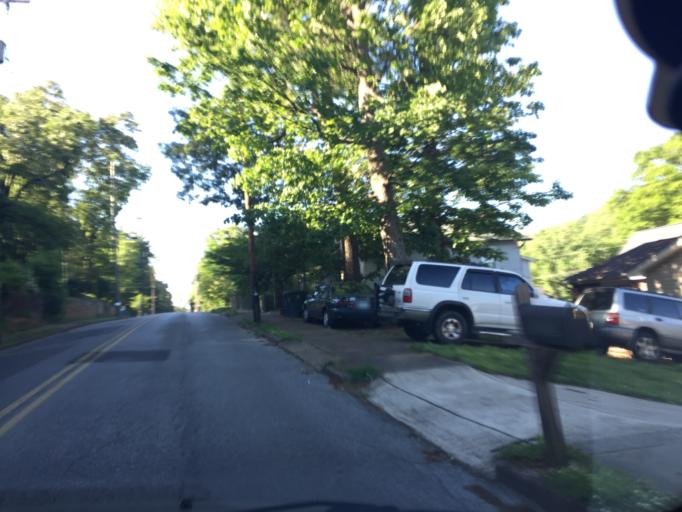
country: US
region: Tennessee
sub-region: Hamilton County
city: Lookout Mountain
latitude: 35.0039
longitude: -85.3275
